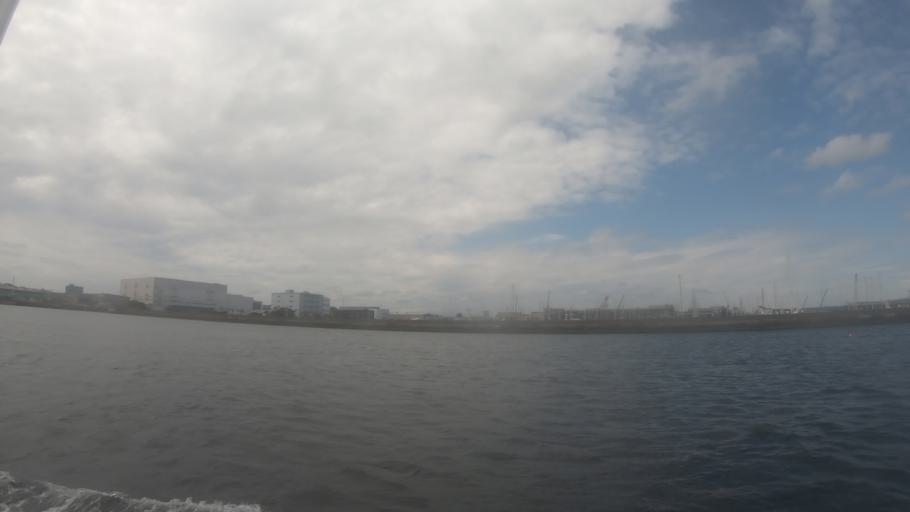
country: JP
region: Kanagawa
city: Yokohama
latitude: 35.3769
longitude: 139.6519
